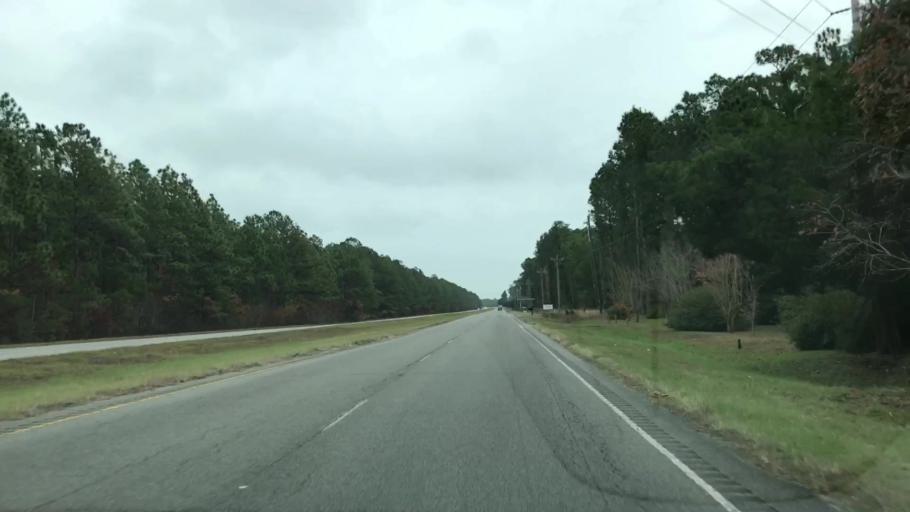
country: US
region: South Carolina
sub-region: Charleston County
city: Awendaw
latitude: 33.0376
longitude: -79.6141
